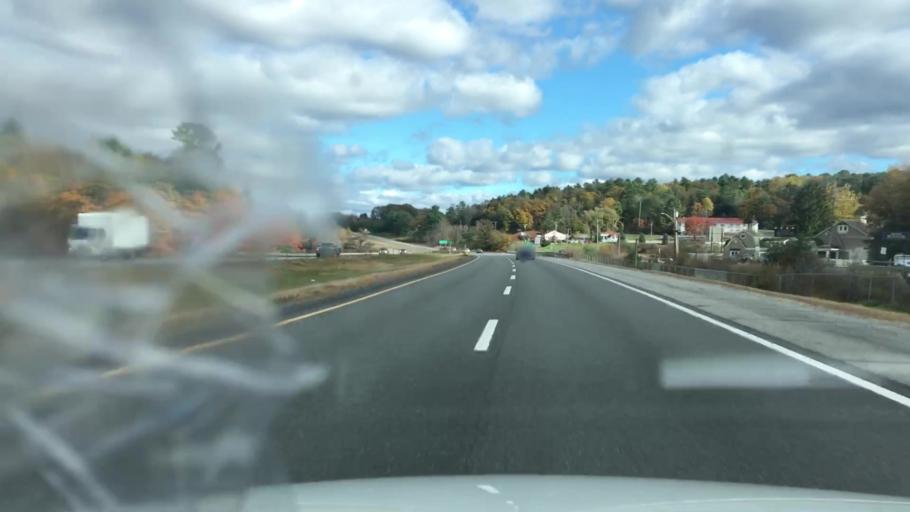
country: US
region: Maine
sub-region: Cumberland County
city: Yarmouth
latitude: 43.8122
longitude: -70.1562
